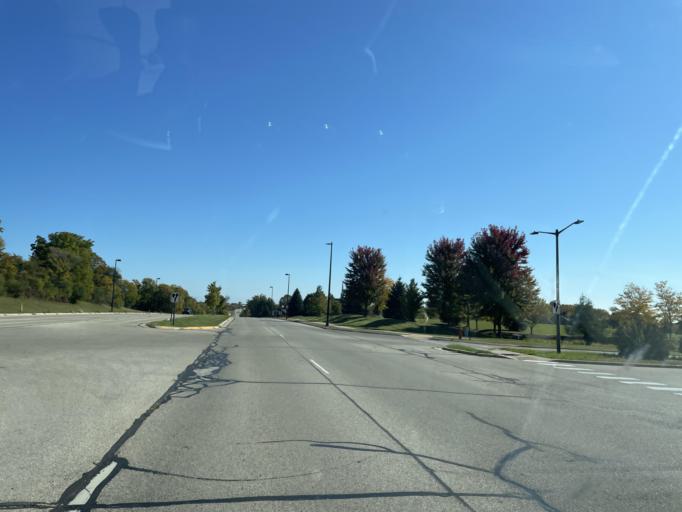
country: US
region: Wisconsin
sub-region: Waukesha County
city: Butler
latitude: 43.1456
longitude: -88.0707
